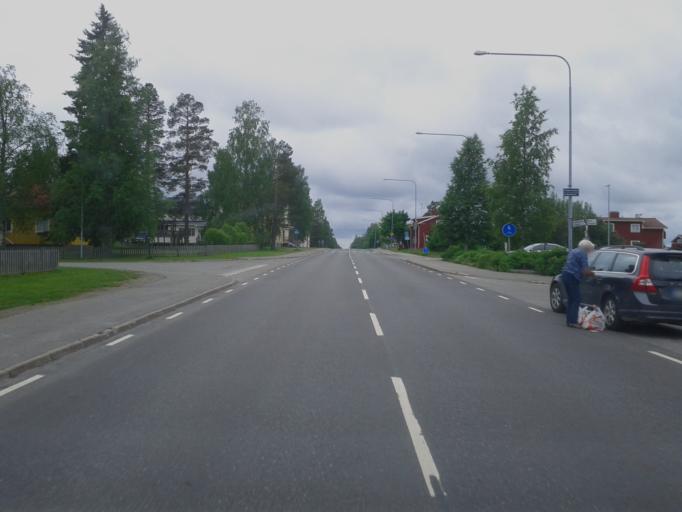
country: SE
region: Vaesterbotten
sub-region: Skelleftea Kommun
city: Boliden
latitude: 64.8669
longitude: 20.3892
